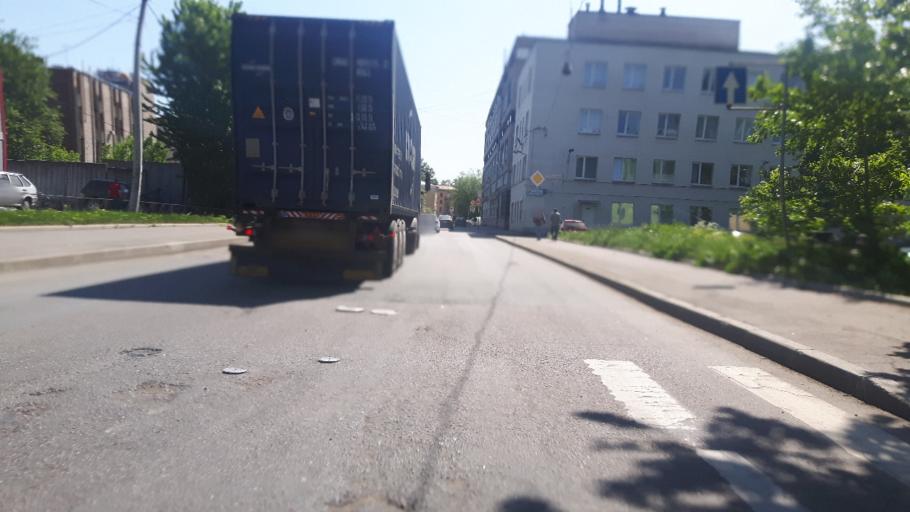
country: RU
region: St.-Petersburg
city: Admiralteisky
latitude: 59.9022
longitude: 30.2841
